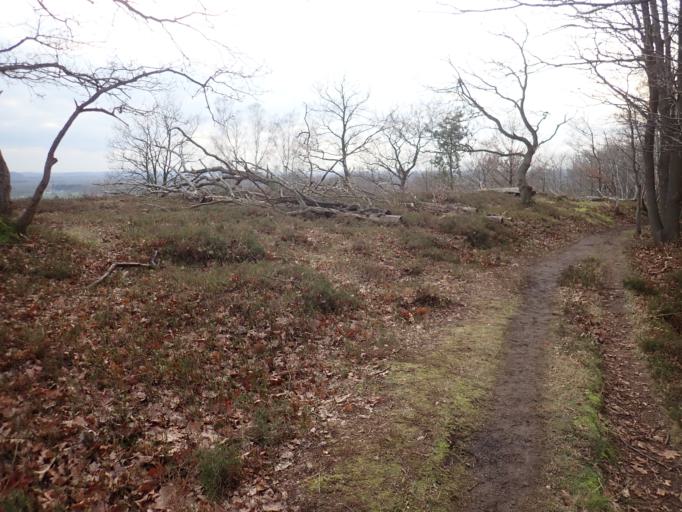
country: BE
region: Flanders
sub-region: Provincie Vlaams-Brabant
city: Holsbeek
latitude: 50.9455
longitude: 4.7854
